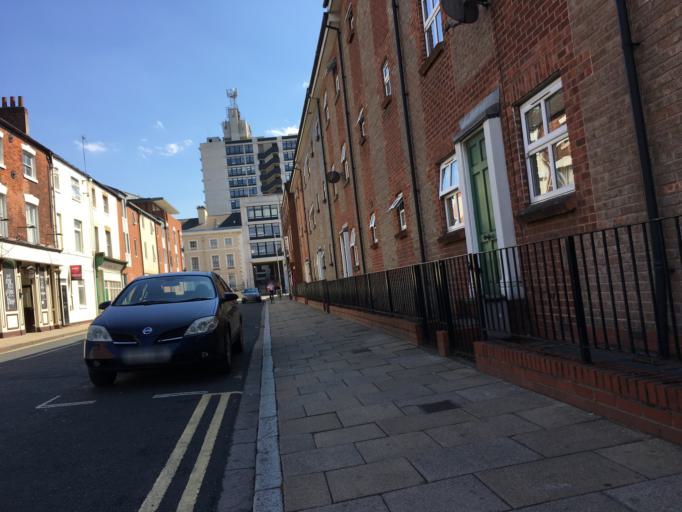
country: GB
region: England
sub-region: City of Kingston upon Hull
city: Hull
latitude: 53.7477
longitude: -0.3397
